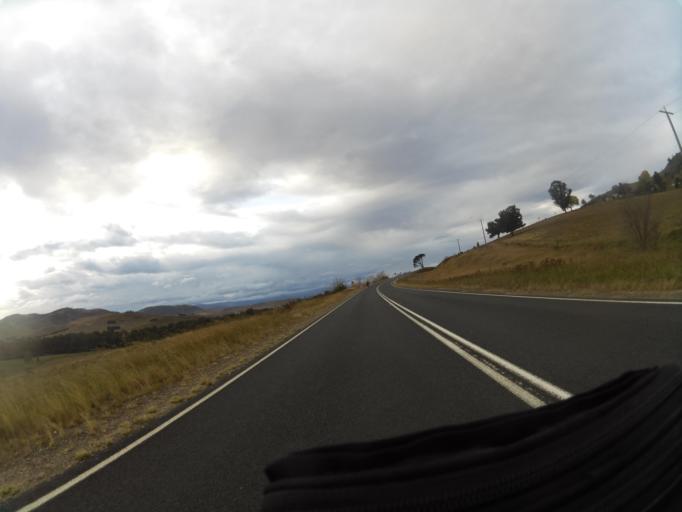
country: AU
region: New South Wales
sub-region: Snowy River
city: Jindabyne
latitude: -36.0832
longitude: 147.9771
